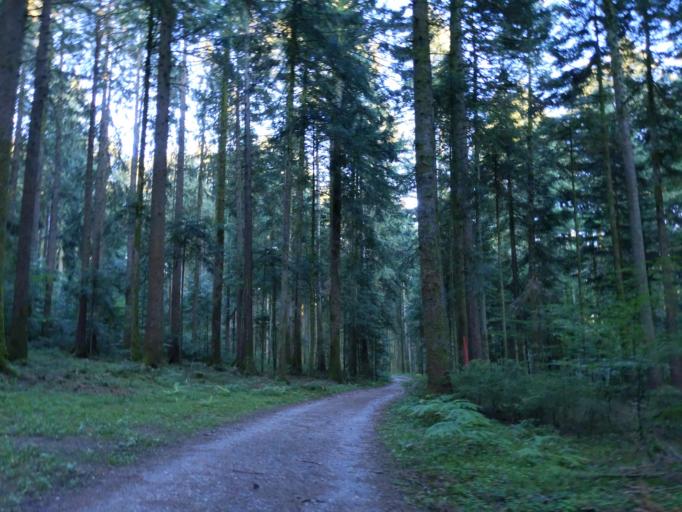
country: DE
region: Baden-Wuerttemberg
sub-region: Karlsruhe Region
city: Alpirsbach
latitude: 48.3372
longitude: 8.4118
